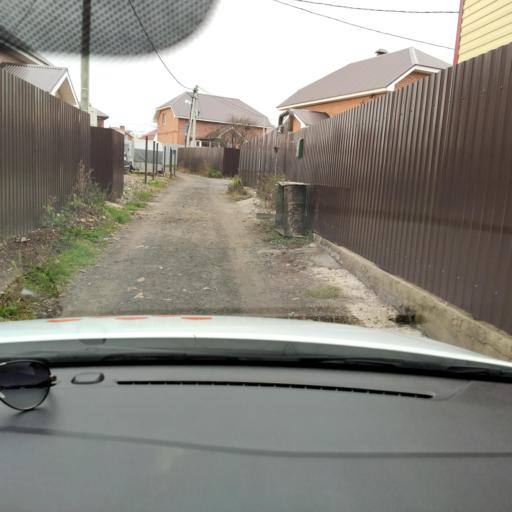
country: RU
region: Tatarstan
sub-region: Gorod Kazan'
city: Kazan
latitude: 55.7919
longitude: 49.2406
